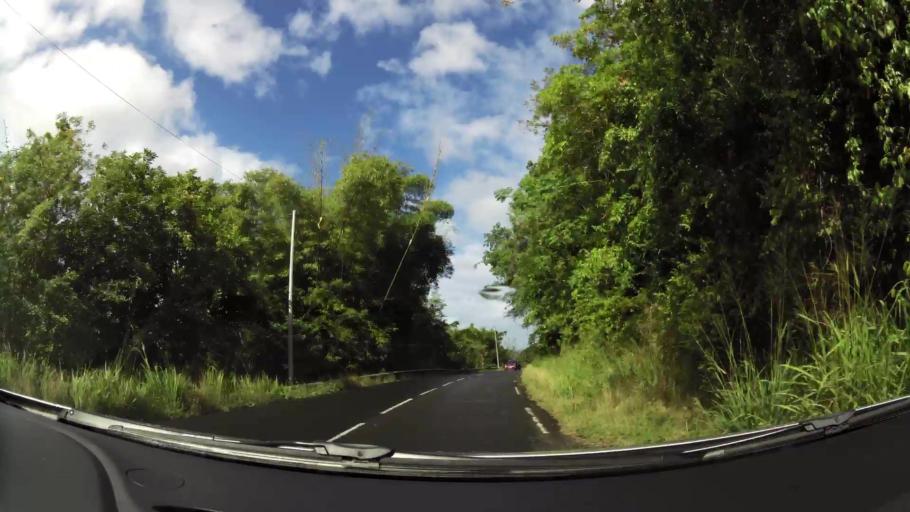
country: MQ
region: Martinique
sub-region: Martinique
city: Les Trois-Ilets
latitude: 14.5353
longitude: -61.0537
